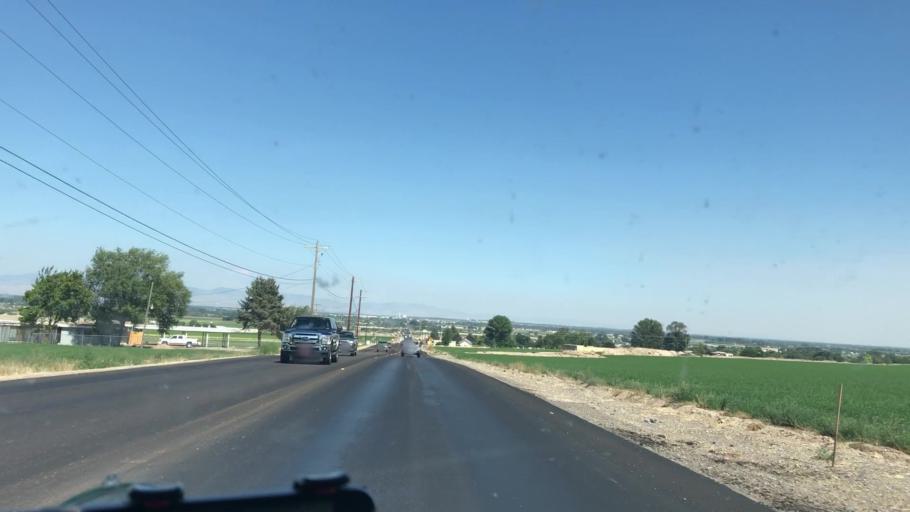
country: US
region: Idaho
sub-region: Canyon County
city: Caldwell
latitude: 43.6043
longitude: -116.6804
